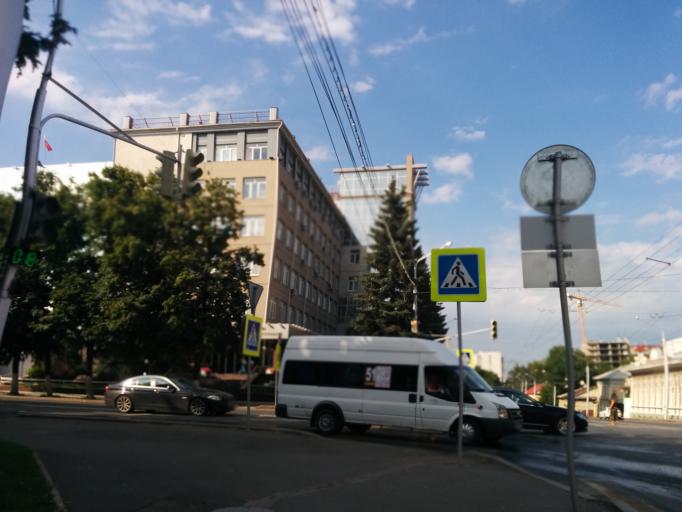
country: RU
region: Bashkortostan
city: Ufa
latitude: 54.7207
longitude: 55.9502
